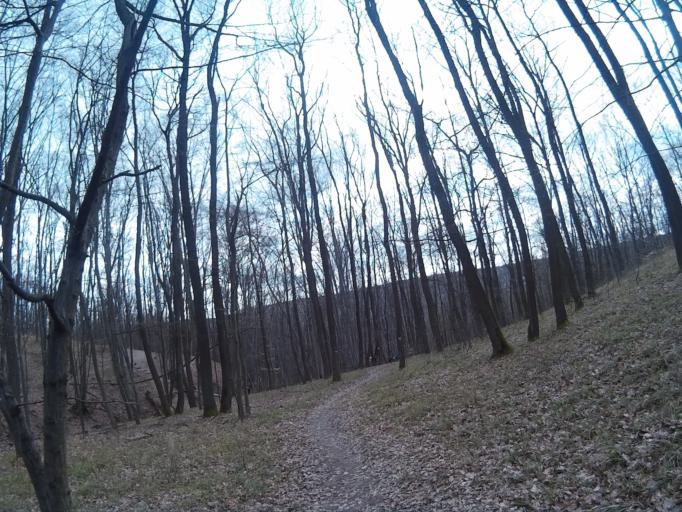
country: HU
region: Pest
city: Kosd
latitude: 47.8446
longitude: 19.1274
